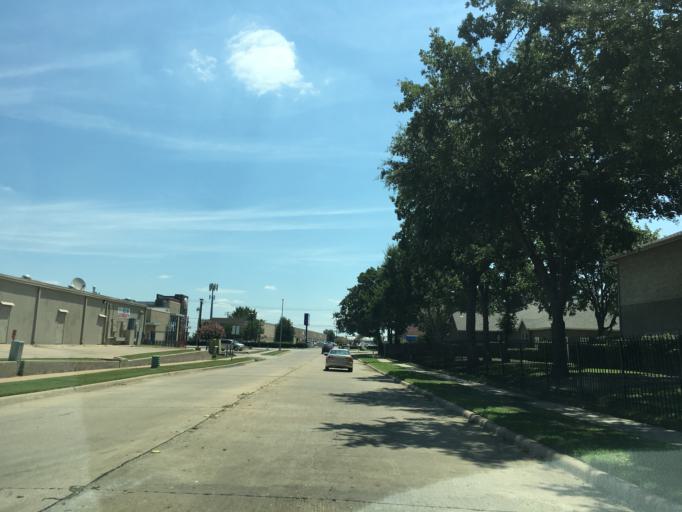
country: US
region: Texas
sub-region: Denton County
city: Lewisville
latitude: 33.0246
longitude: -96.9944
